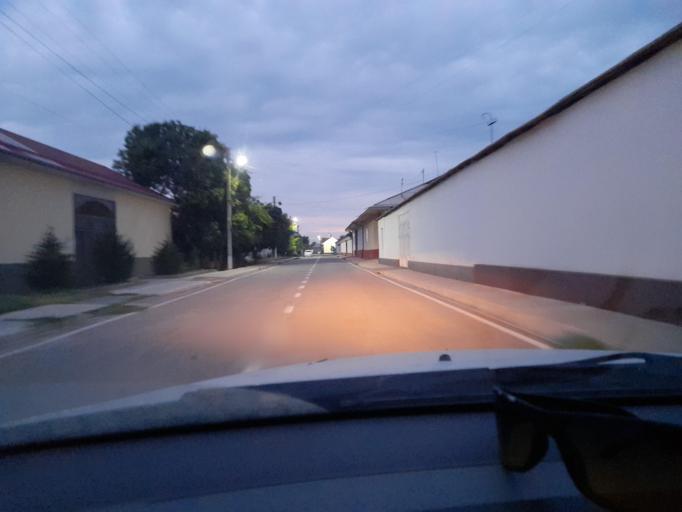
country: UZ
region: Sirdaryo
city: Guliston
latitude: 40.5012
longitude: 68.7823
